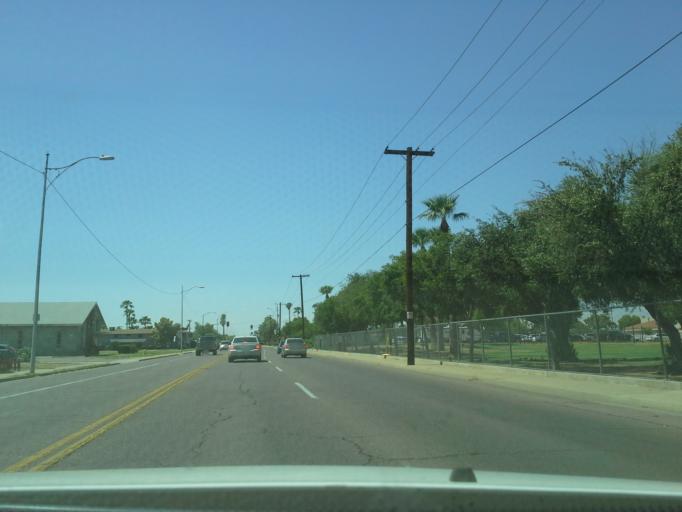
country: US
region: Arizona
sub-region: Maricopa County
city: Phoenix
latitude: 33.4878
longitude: -112.0893
